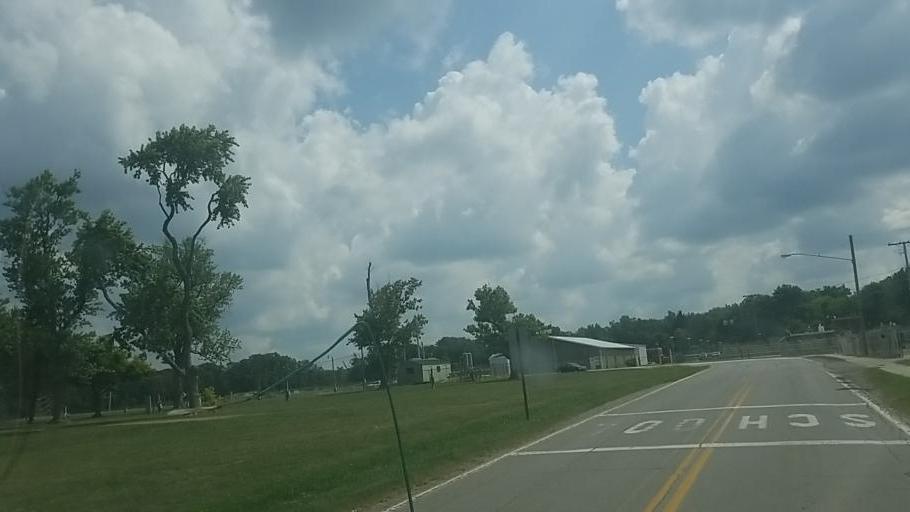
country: US
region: Ohio
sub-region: Wyandot County
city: Upper Sandusky
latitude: 40.8421
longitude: -83.2793
